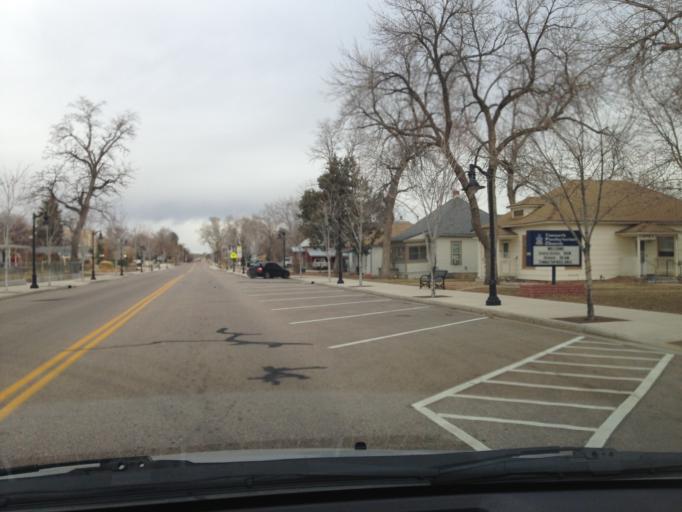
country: US
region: Colorado
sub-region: Weld County
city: Windsor
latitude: 40.5302
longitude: -104.9823
